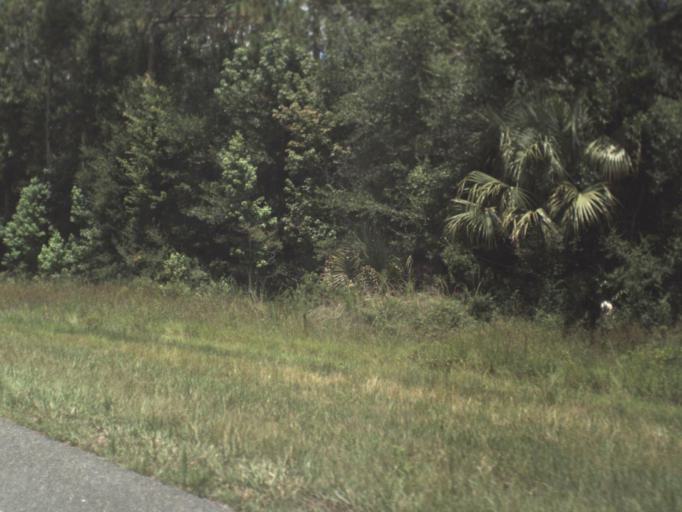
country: US
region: Florida
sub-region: Taylor County
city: Perry
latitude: 30.1427
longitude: -83.7862
